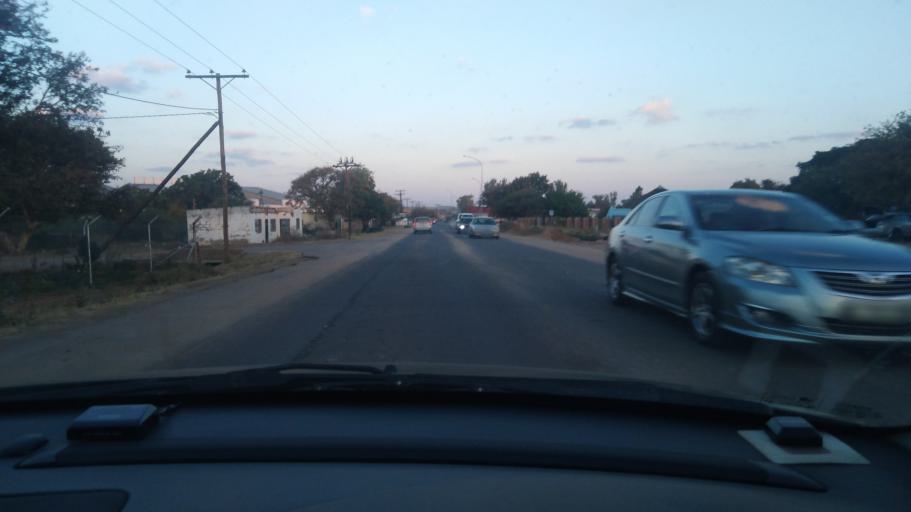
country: BW
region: Central
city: Mahalapye
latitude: -23.1035
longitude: 26.8304
